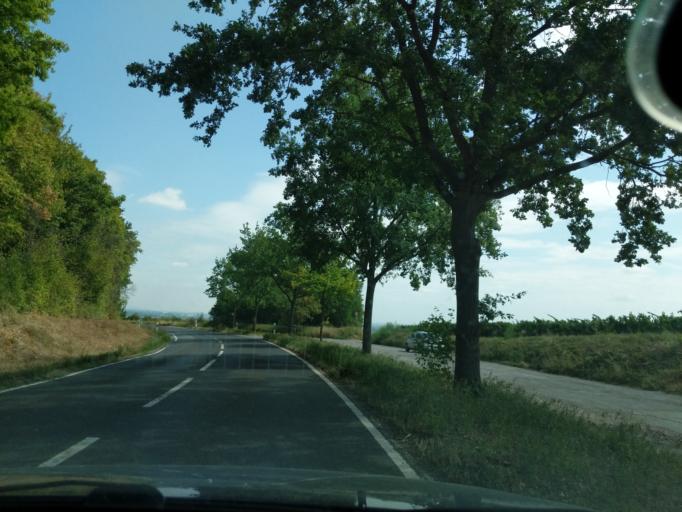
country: DE
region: Rheinland-Pfalz
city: Mainz
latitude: 49.9652
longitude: 8.3026
